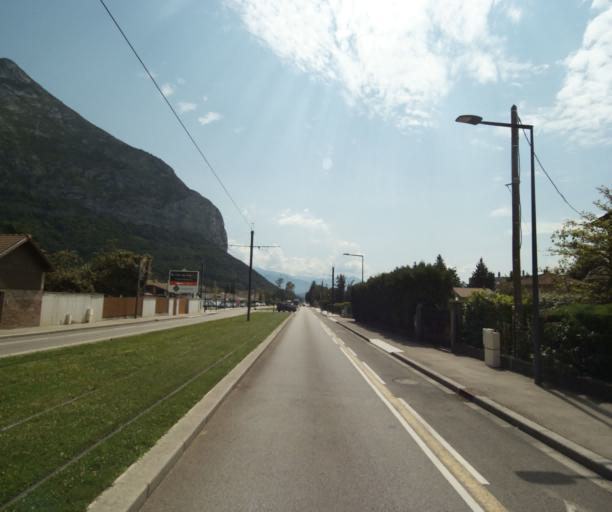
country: FR
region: Rhone-Alpes
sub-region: Departement de l'Isere
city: Saint-Egreve
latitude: 45.2269
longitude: 5.6854
